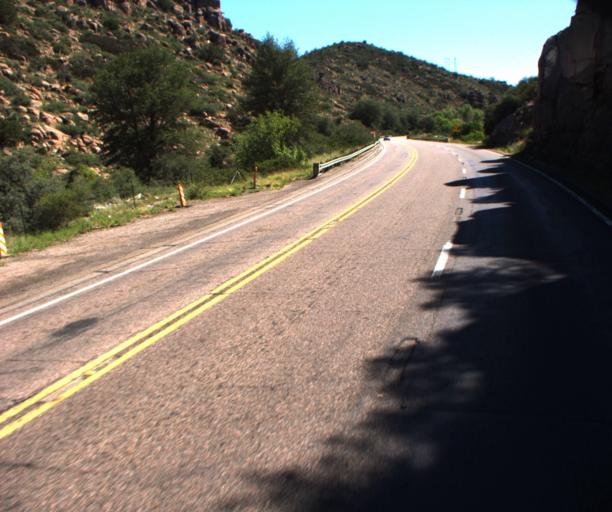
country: US
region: Arizona
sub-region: Pinal County
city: Superior
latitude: 33.3399
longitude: -111.0169
